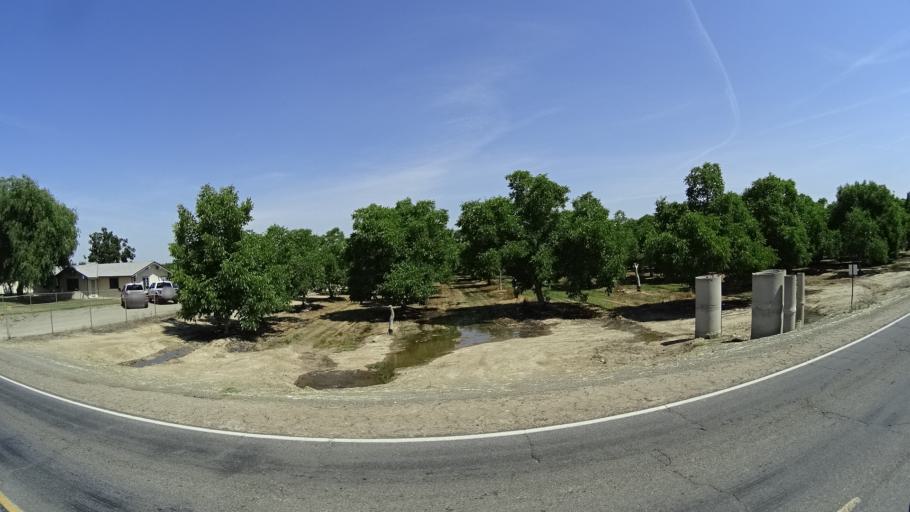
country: US
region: California
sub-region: Fresno County
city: Riverdale
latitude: 36.4021
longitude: -119.8049
